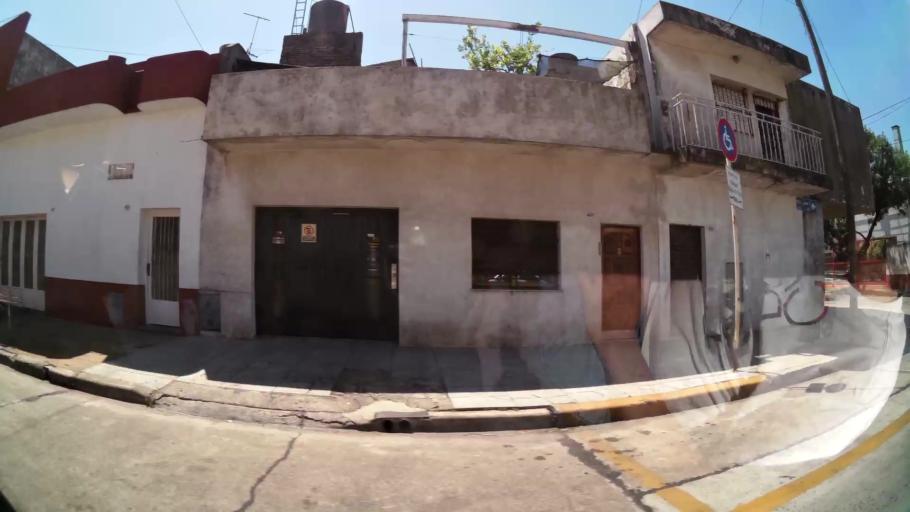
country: AR
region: Buenos Aires
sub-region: Partido de Avellaneda
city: Avellaneda
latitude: -34.6557
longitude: -58.4096
